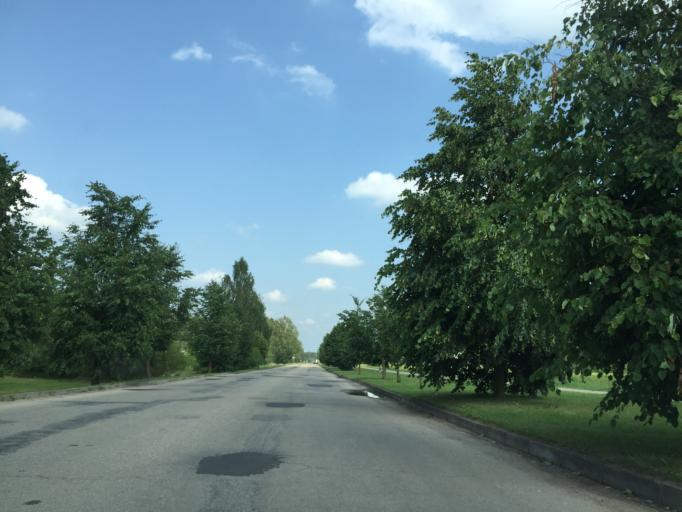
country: LV
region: Jelgava
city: Jelgava
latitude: 56.6708
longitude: 23.7440
